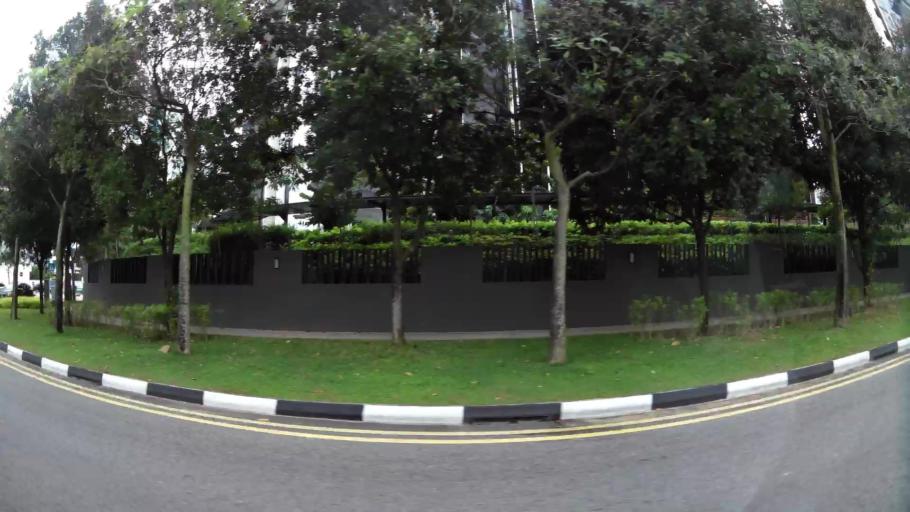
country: MY
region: Johor
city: Kampung Pasir Gudang Baru
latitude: 1.4011
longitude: 103.9086
